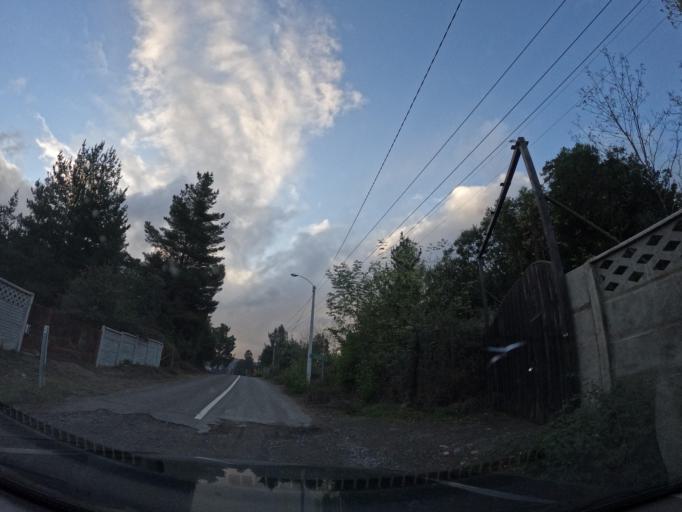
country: CL
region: Biobio
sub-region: Provincia de Concepcion
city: Chiguayante
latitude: -37.0589
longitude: -72.9533
